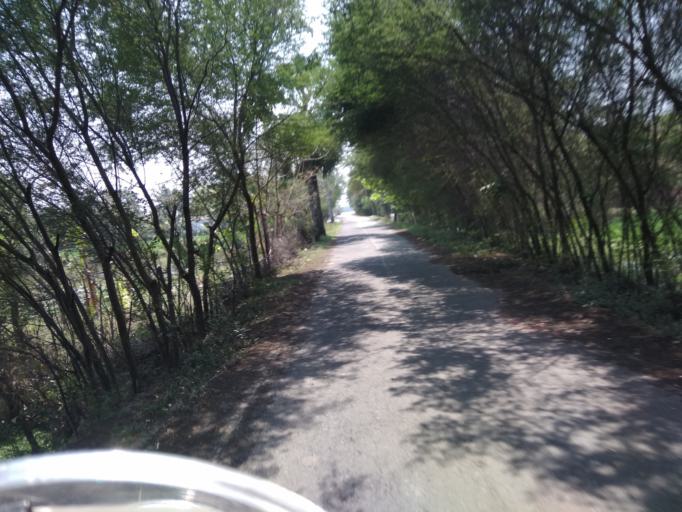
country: BD
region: Khulna
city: Satkhira
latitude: 22.4032
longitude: 89.2136
